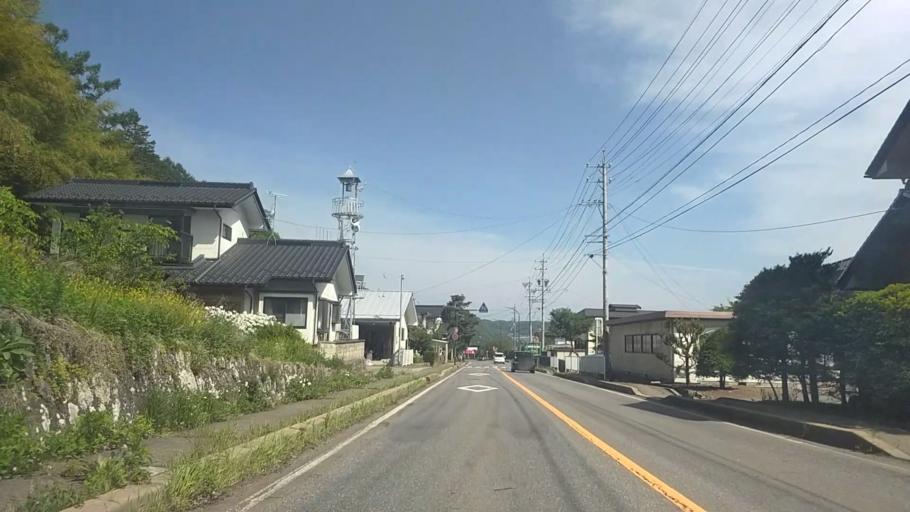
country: JP
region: Nagano
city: Saku
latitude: 36.1085
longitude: 138.4783
